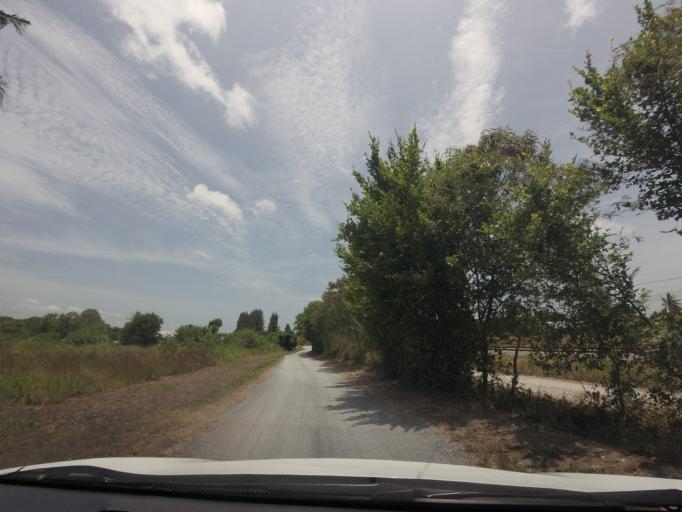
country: TH
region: Chon Buri
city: Chon Buri
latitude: 13.3213
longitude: 100.9791
